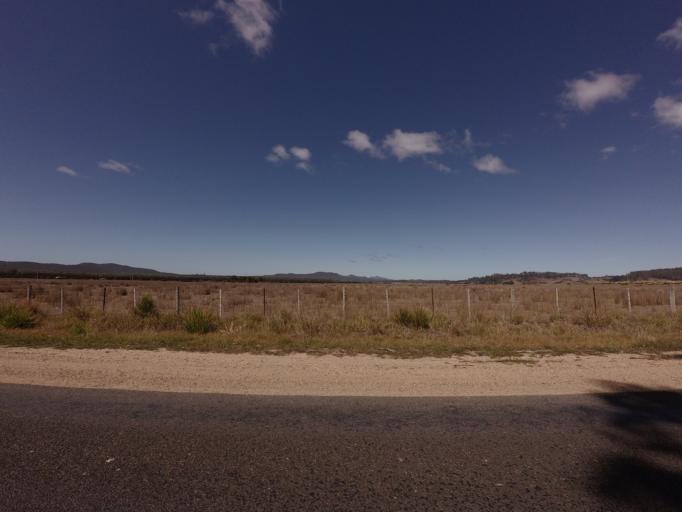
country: AU
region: Tasmania
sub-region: Break O'Day
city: St Helens
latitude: -41.9498
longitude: 148.1959
